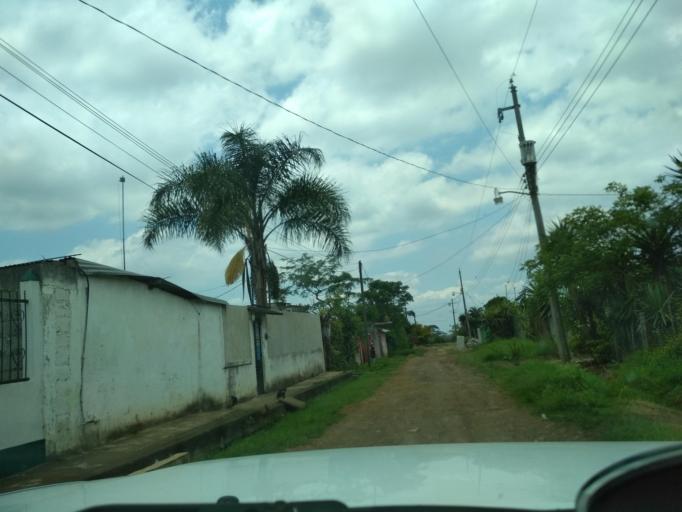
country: MX
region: Veracruz
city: Tocuila
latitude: 18.9504
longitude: -97.0169
